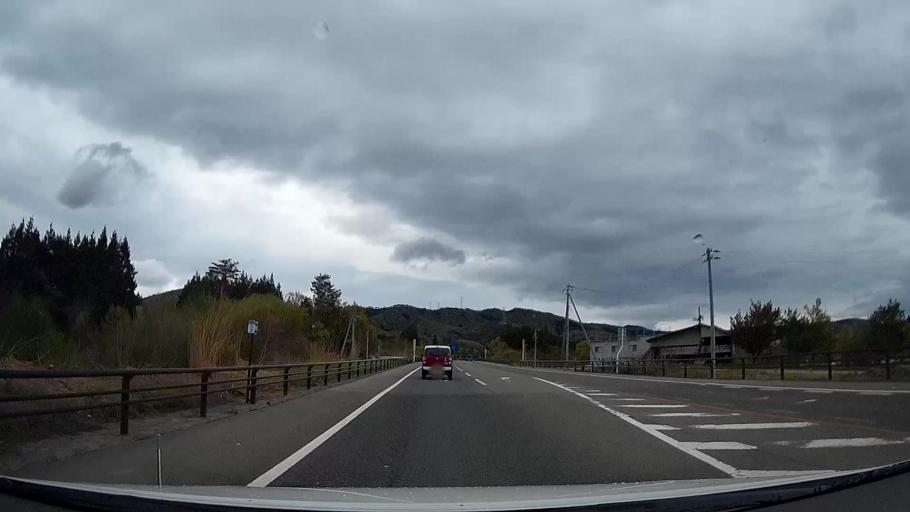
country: JP
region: Yamagata
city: Kaminoyama
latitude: 38.1124
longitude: 140.2110
